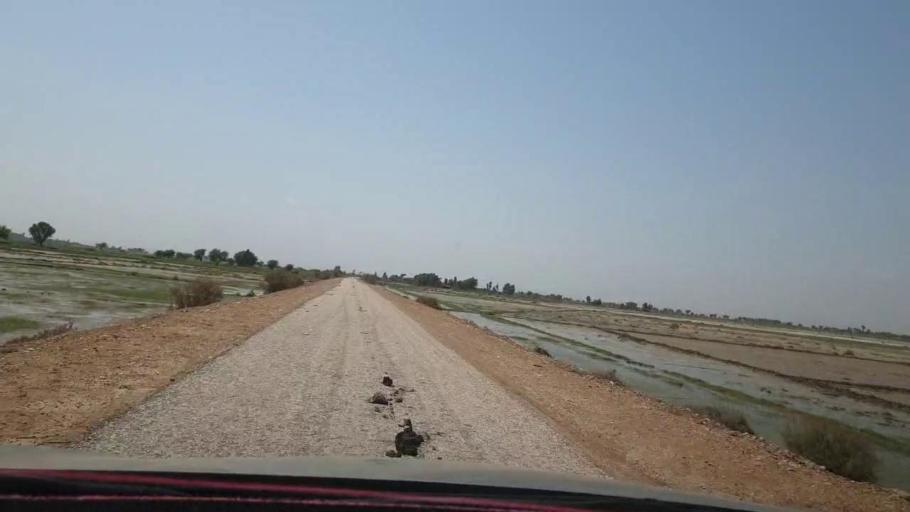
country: PK
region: Sindh
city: Warah
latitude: 27.5080
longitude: 67.7217
